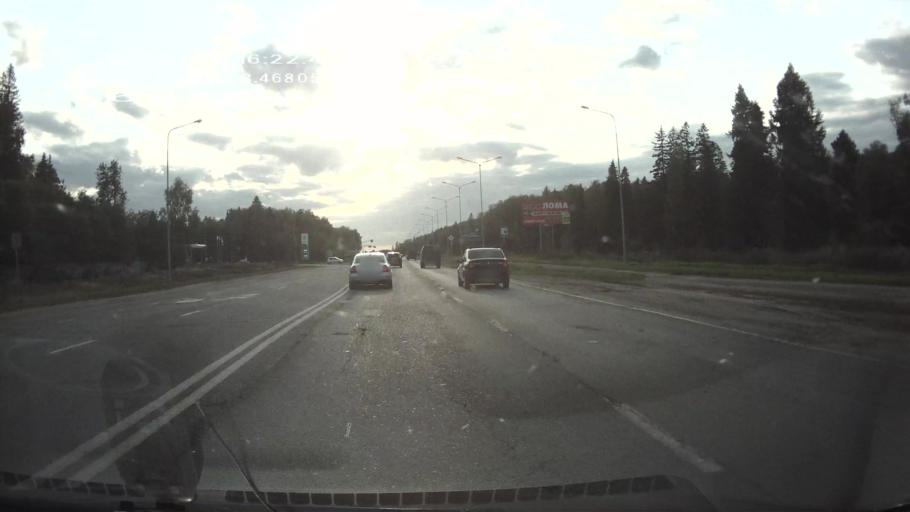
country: RU
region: Mariy-El
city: Sovetskiy
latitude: 56.7516
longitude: 48.4657
